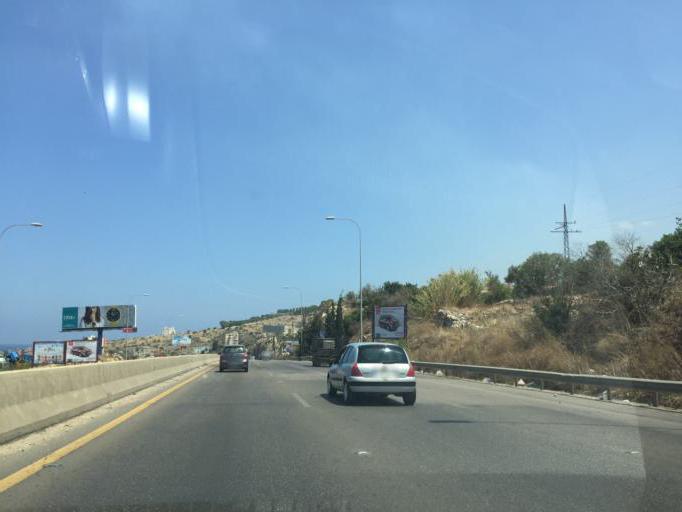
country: LB
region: Liban-Sud
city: Sidon
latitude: 33.6683
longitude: 35.4282
